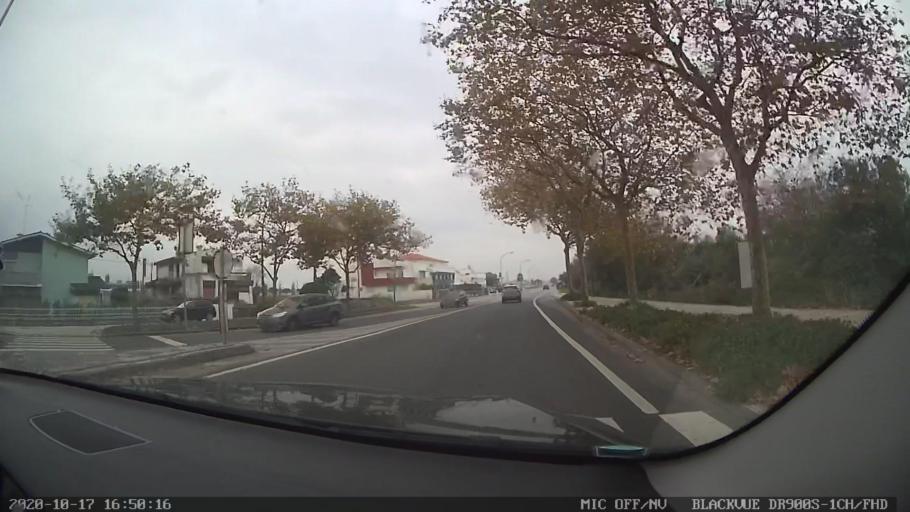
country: PT
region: Braga
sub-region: Esposende
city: Esposende
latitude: 41.5251
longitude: -8.7766
